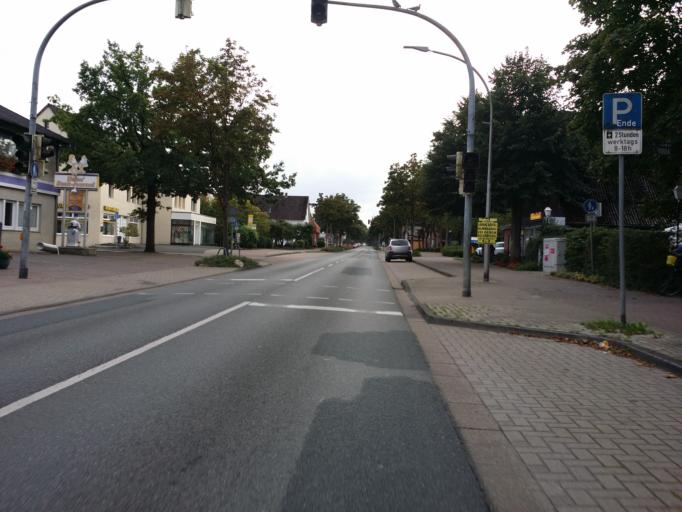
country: DE
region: Lower Saxony
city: Bremervorde
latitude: 53.4800
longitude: 9.1404
